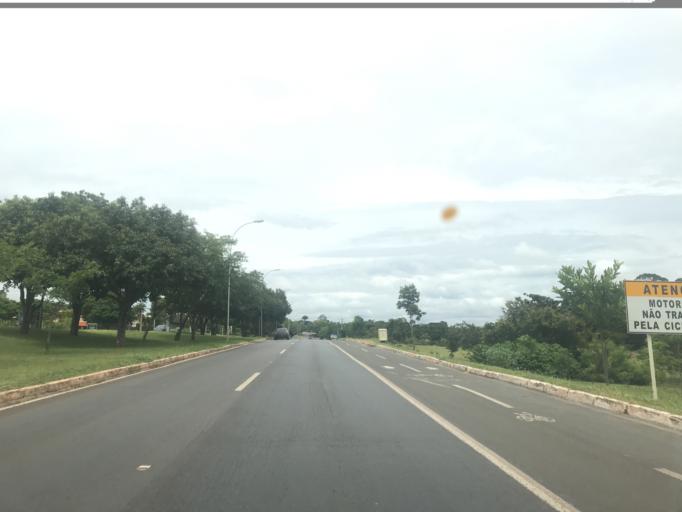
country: BR
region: Federal District
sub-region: Brasilia
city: Brasilia
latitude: -15.8346
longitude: -47.8270
